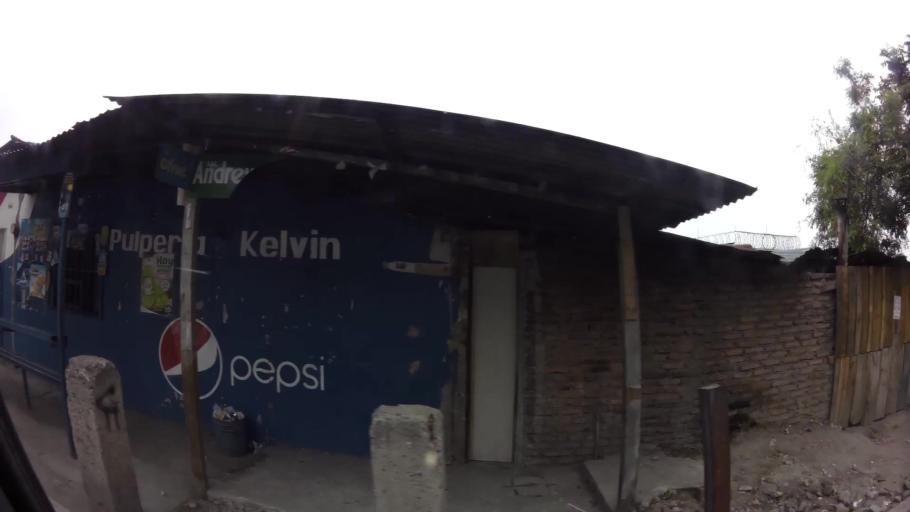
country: HN
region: Francisco Morazan
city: Tegucigalpa
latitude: 14.0750
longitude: -87.2296
